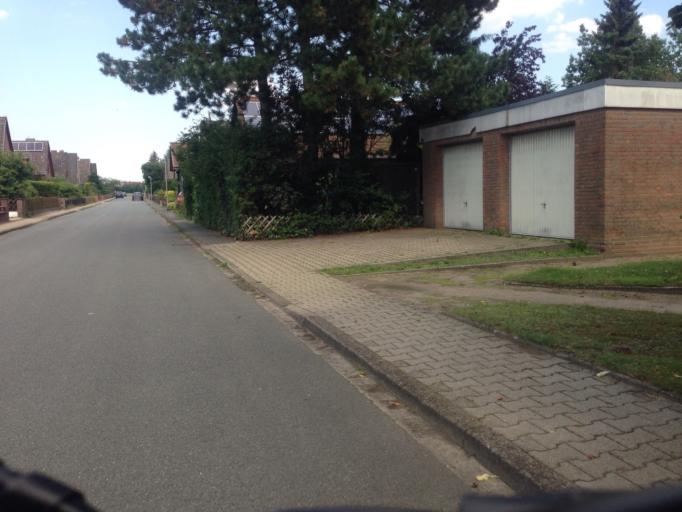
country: DE
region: Lower Saxony
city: Adendorf
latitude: 53.2819
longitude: 10.4375
